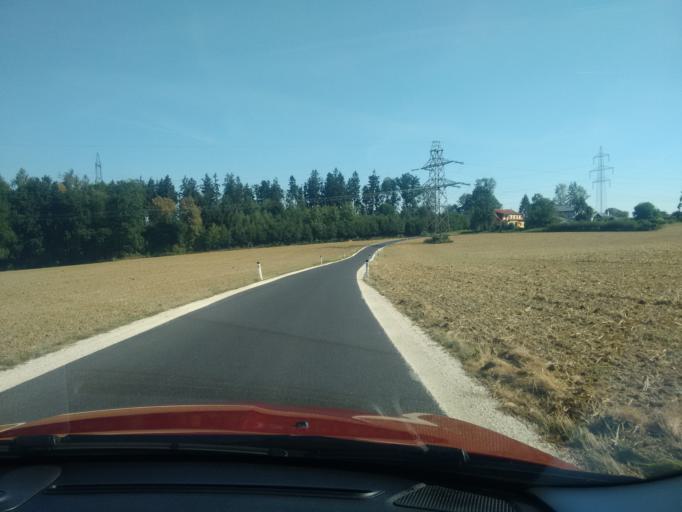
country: AT
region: Upper Austria
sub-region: Wels-Land
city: Sattledt
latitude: 48.0831
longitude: 14.0717
